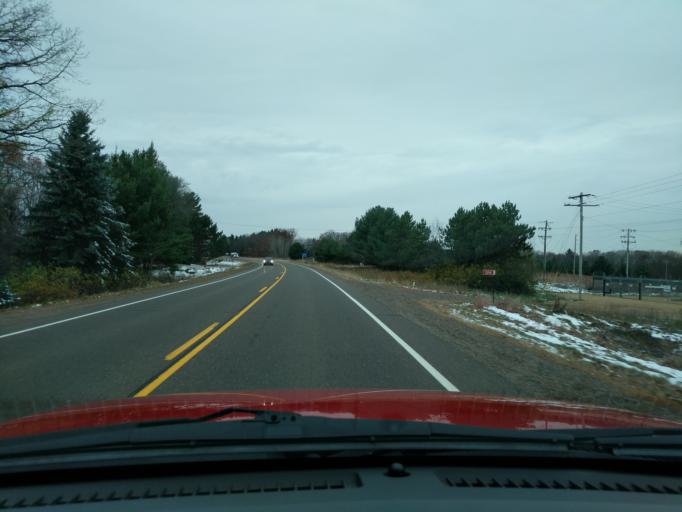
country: US
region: Wisconsin
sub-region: Burnett County
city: Siren
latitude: 45.8233
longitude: -92.2516
